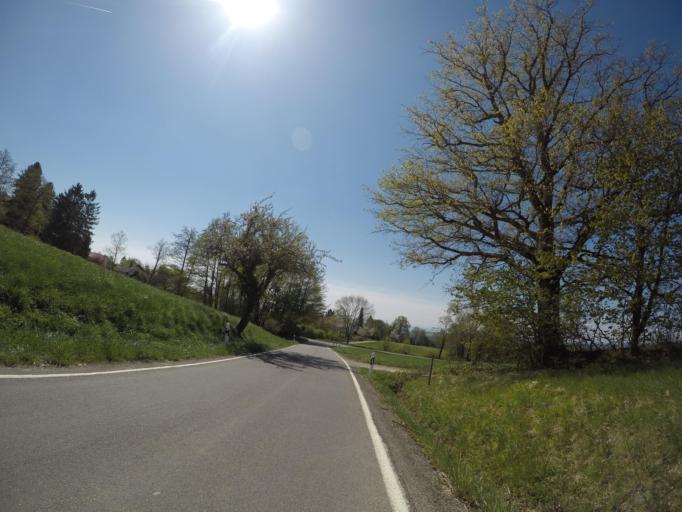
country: DE
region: Baden-Wuerttemberg
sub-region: Tuebingen Region
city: Markdorf
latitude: 47.7373
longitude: 9.3833
